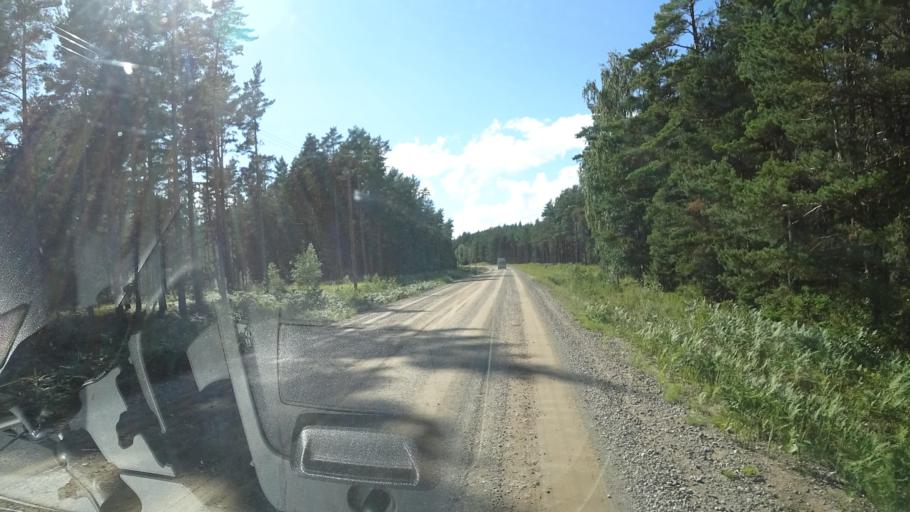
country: LV
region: Ventspils
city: Ventspils
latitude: 57.4881
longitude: 21.6715
